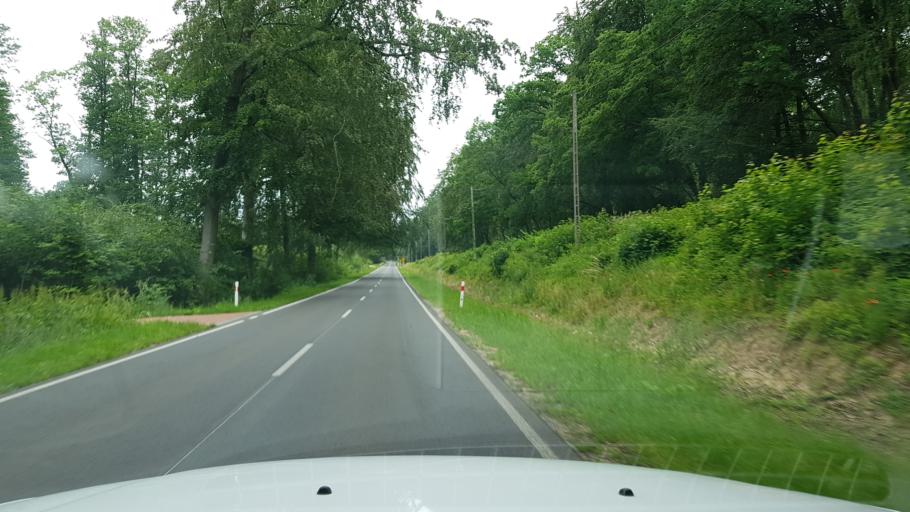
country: PL
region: West Pomeranian Voivodeship
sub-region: Powiat gryficki
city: Gryfice
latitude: 53.9052
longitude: 15.1464
